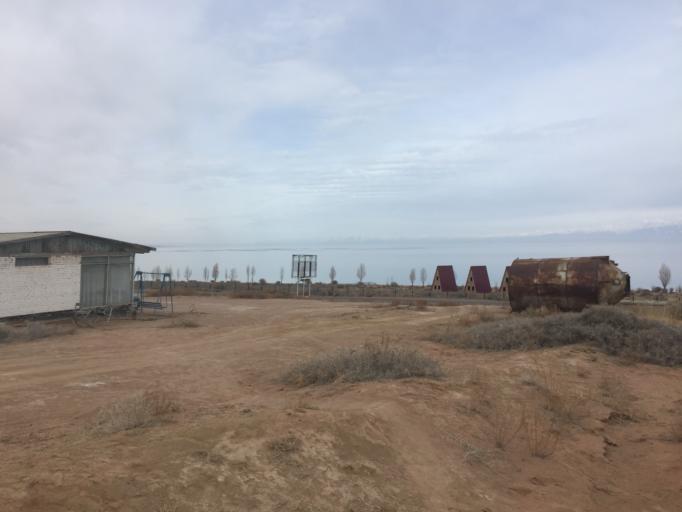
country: KG
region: Ysyk-Koel
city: Kadzhi-Say
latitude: 42.1625
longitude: 77.1636
